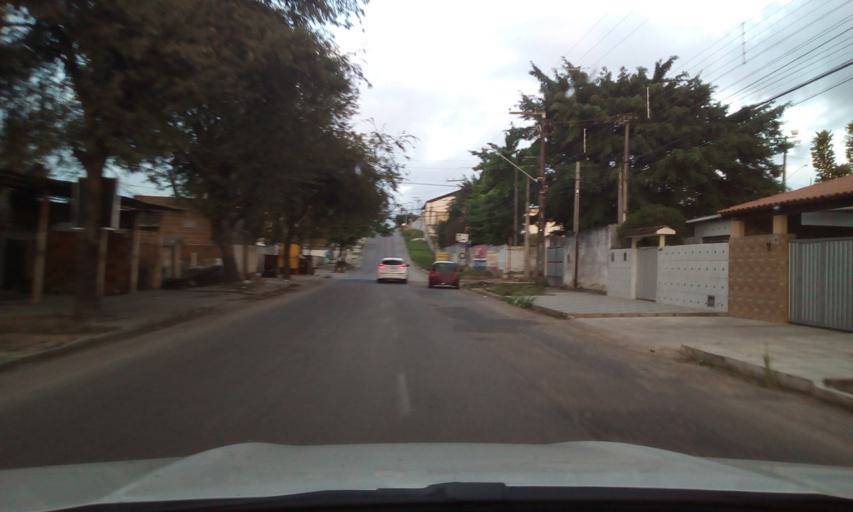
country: BR
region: Paraiba
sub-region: Joao Pessoa
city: Joao Pessoa
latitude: -7.1767
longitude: -34.8831
